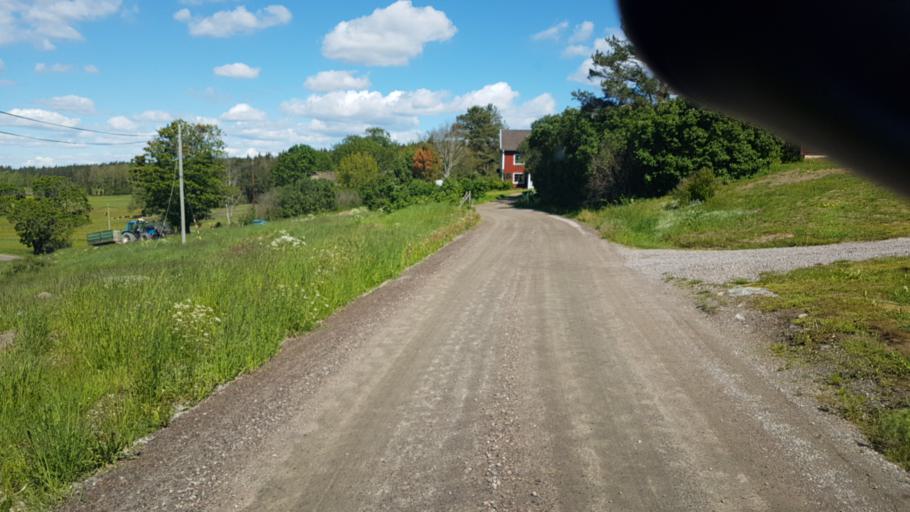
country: SE
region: Vaermland
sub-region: Grums Kommun
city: Grums
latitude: 59.5349
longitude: 12.8854
